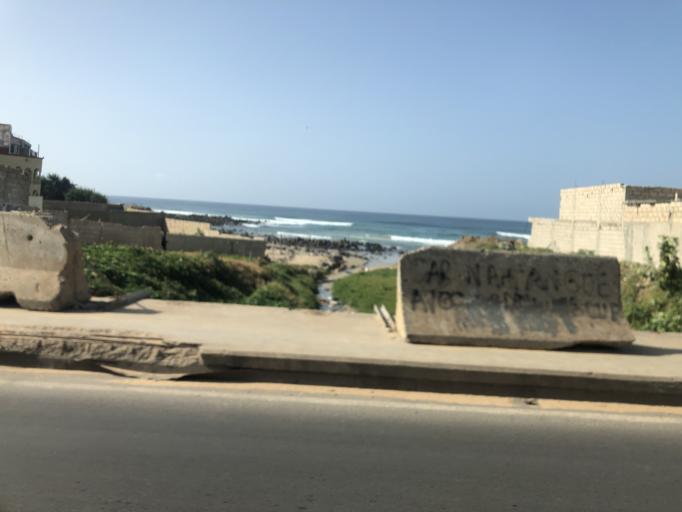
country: SN
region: Dakar
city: Mermoz Boabab
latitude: 14.7536
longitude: -17.4973
